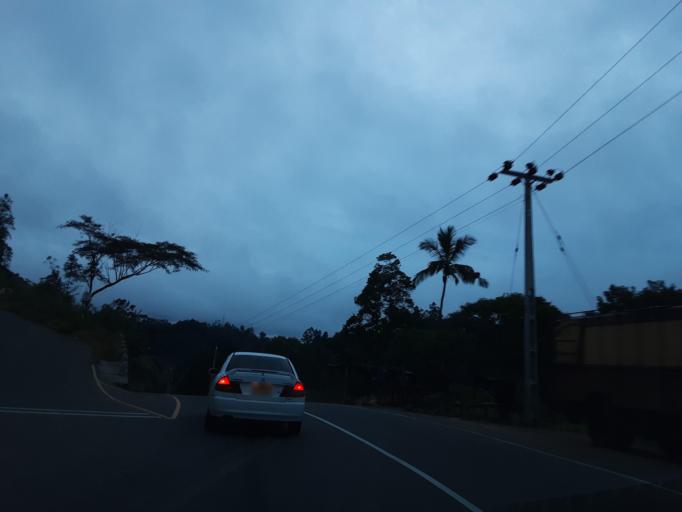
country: LK
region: Uva
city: Haputale
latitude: 6.9108
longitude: 80.9295
